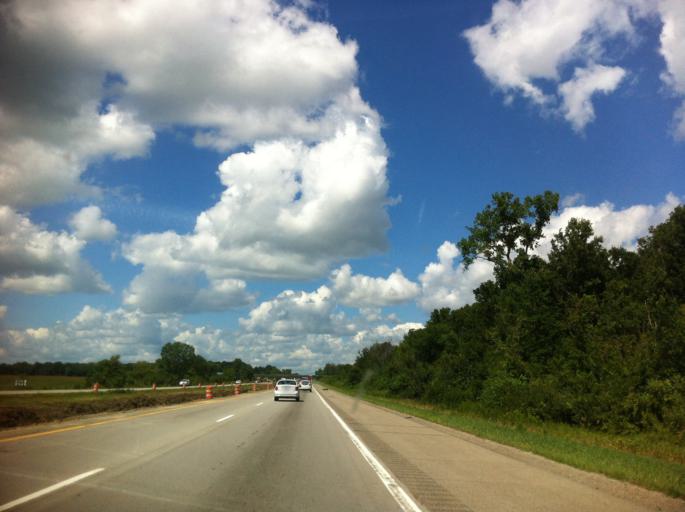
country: US
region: Michigan
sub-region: Washtenaw County
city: Milan
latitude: 42.1253
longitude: -83.6828
